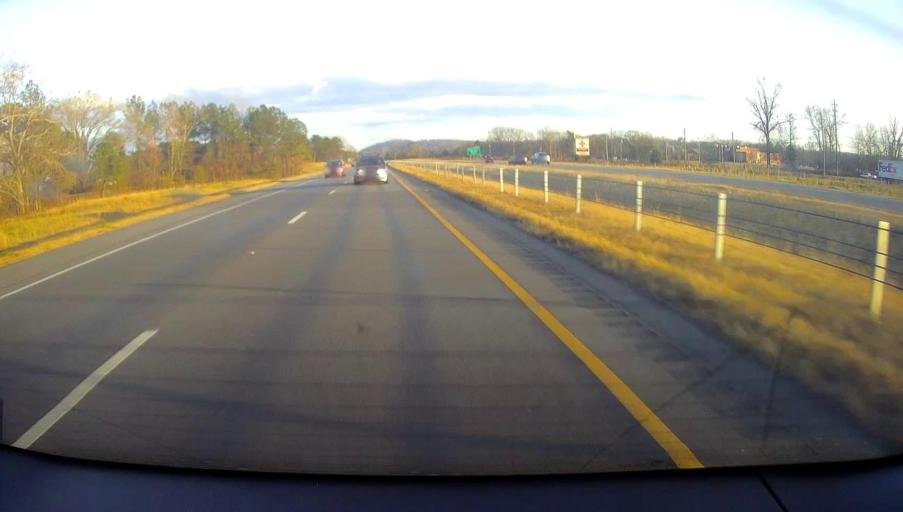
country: US
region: Alabama
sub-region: Etowah County
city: Rainbow City
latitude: 33.9966
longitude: -86.0514
